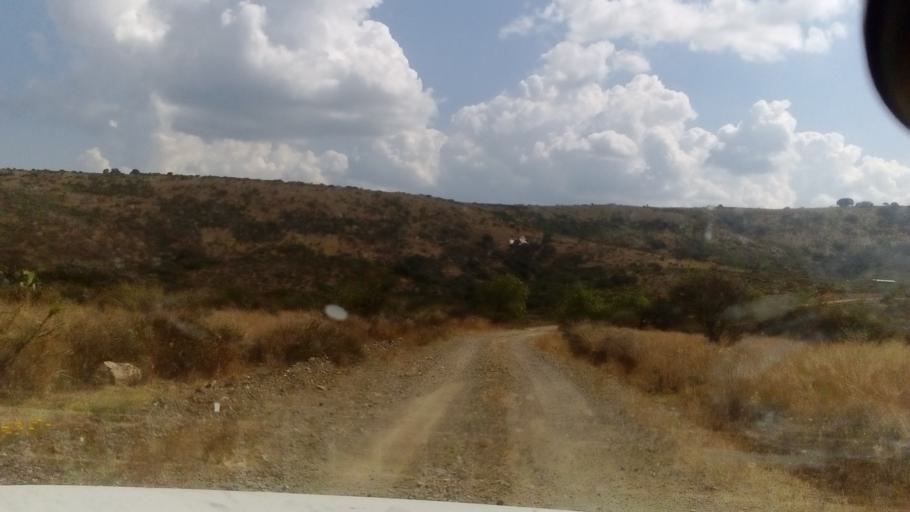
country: MX
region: Guanajuato
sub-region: Silao de la Victoria
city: San Francisco (Banos de Agua Caliente)
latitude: 21.1865
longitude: -101.4608
